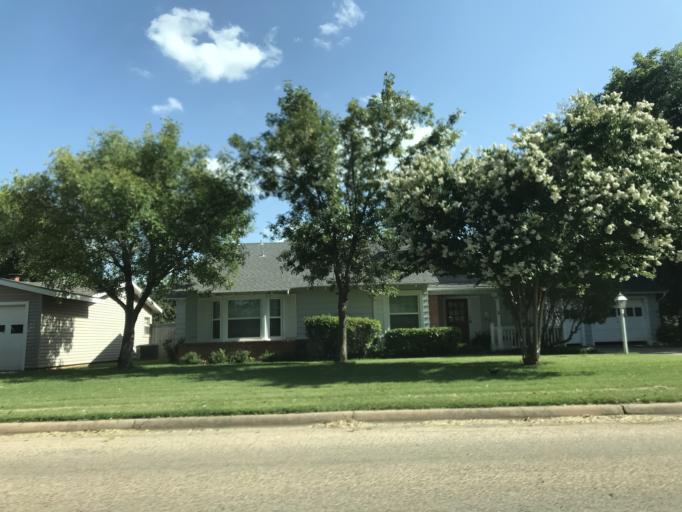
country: US
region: Texas
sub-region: Taylor County
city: Abilene
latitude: 32.4302
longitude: -99.7655
